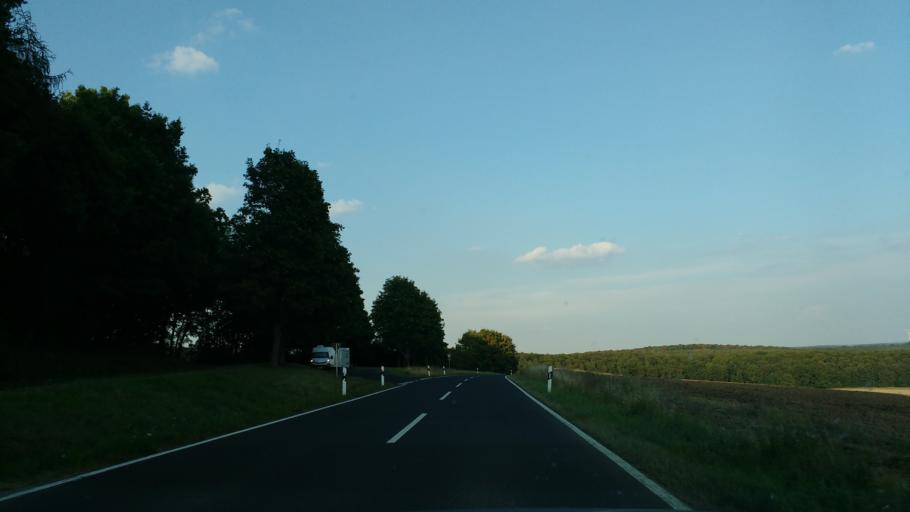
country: DE
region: Bavaria
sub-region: Regierungsbezirk Unterfranken
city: Fuchsstadt
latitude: 50.0915
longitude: 9.9562
